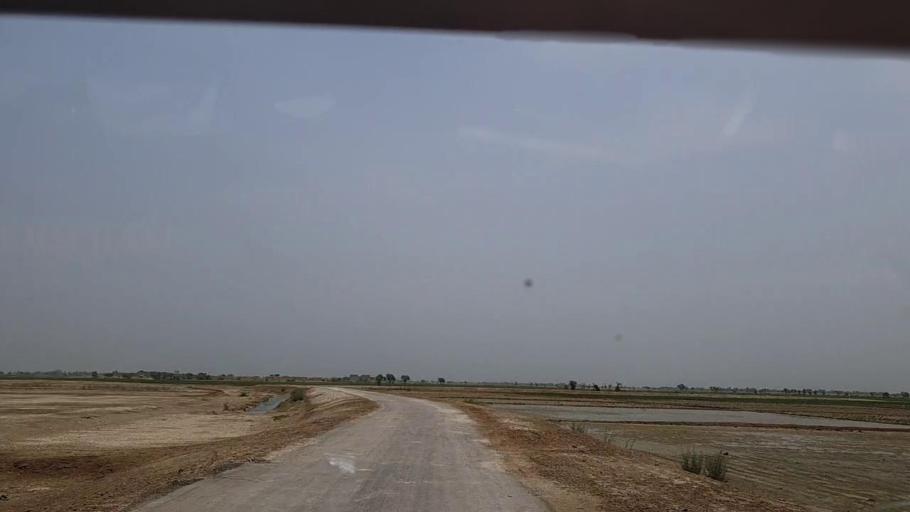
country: PK
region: Sindh
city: Khairpur Nathan Shah
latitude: 27.0177
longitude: 67.6485
